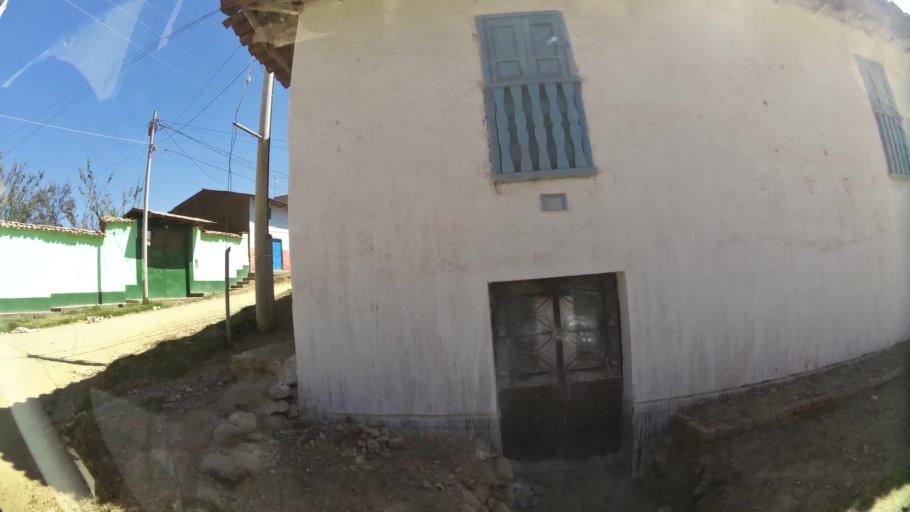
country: PE
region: Junin
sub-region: Provincia de Concepcion
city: Concepcion
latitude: -11.9215
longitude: -75.3136
